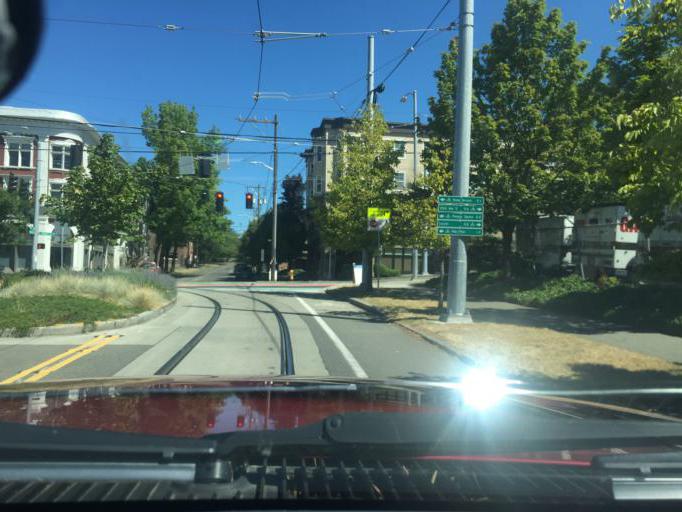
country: US
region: Washington
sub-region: King County
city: Seattle
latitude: 47.6013
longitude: -122.3141
